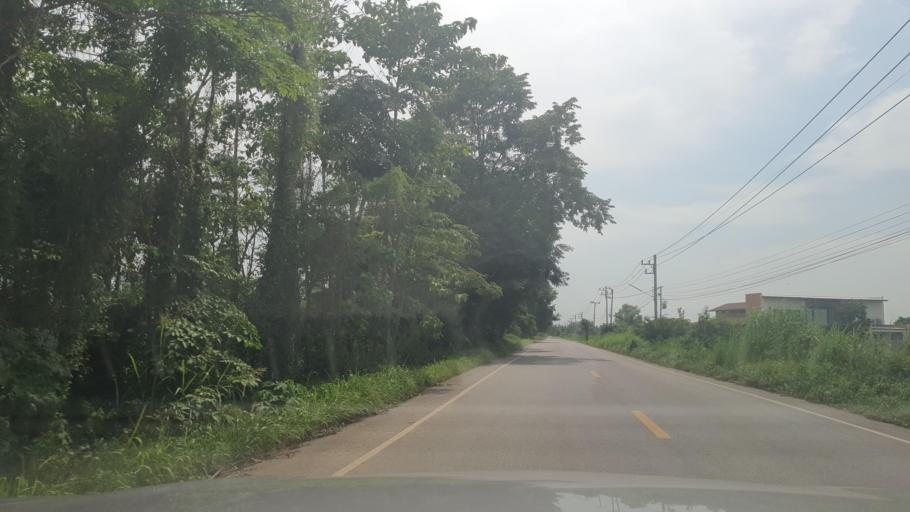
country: TH
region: Sukhothai
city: Si Samrong
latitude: 17.1195
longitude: 99.8638
